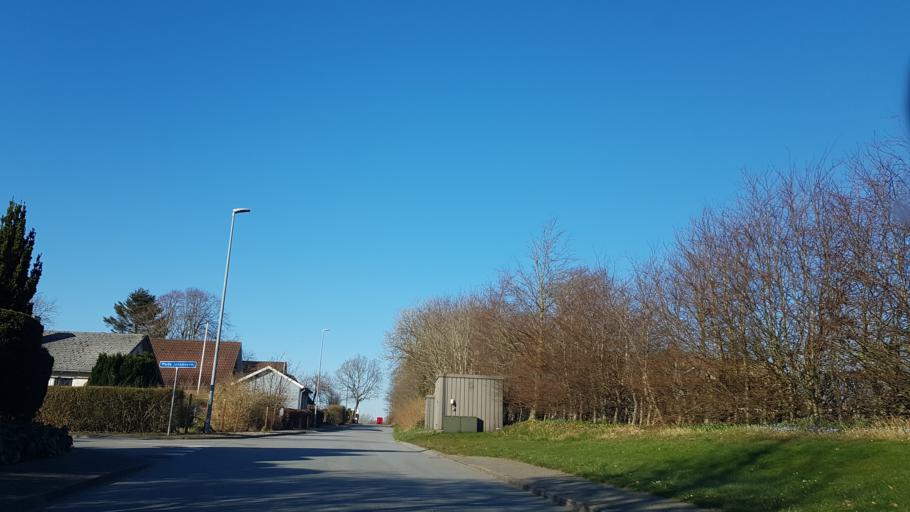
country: DK
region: South Denmark
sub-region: Vejen Kommune
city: Brorup
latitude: 55.4093
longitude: 8.9696
